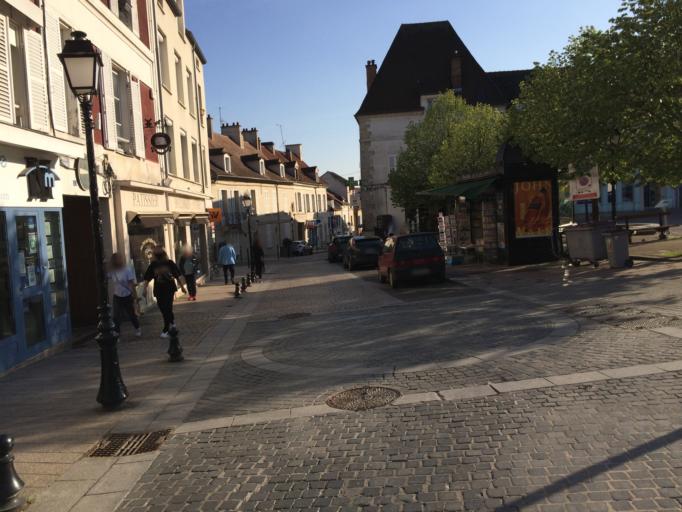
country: FR
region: Ile-de-France
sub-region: Departement de l'Essonne
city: Villebon-sur-Yvette
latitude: 48.7124
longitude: 2.2435
